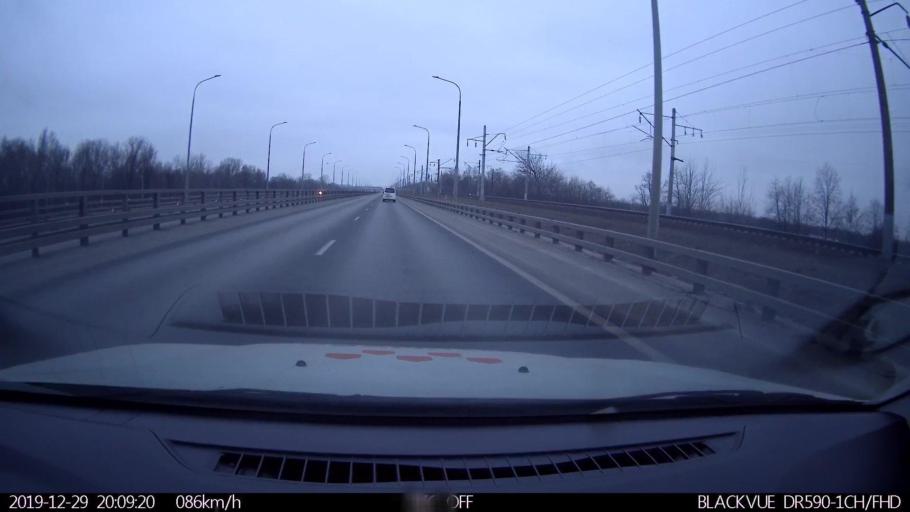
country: RU
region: Nizjnij Novgorod
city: Neklyudovo
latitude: 56.3765
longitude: 43.9531
